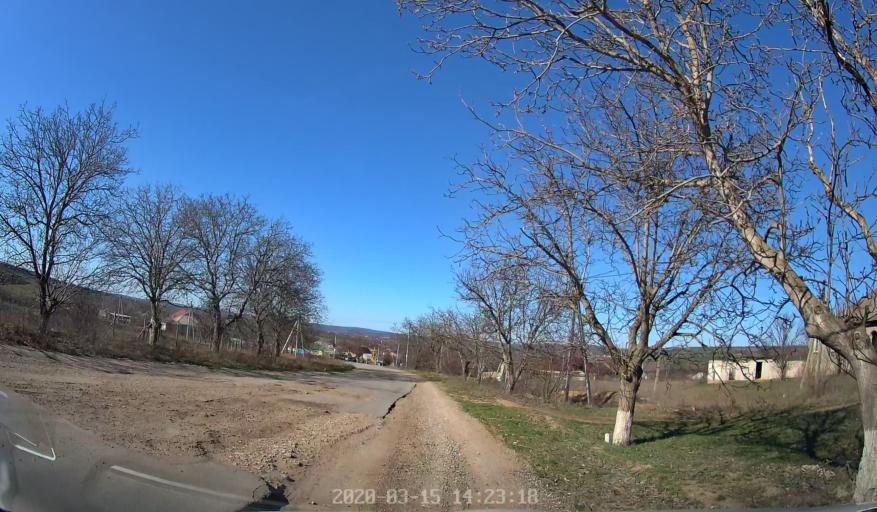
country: MD
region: Orhei
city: Orhei
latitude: 47.3298
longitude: 28.9245
